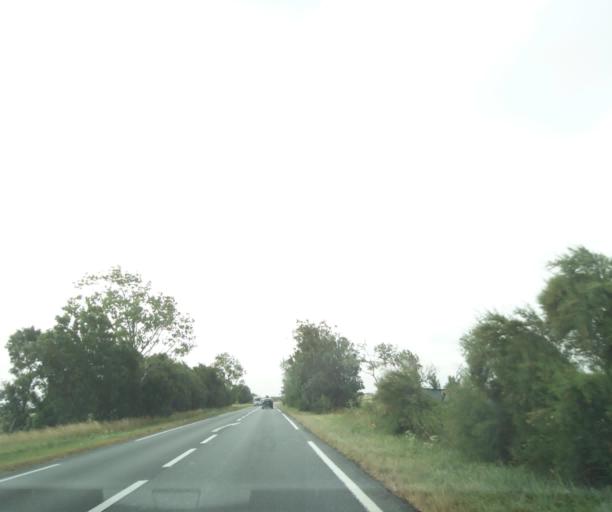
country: FR
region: Poitou-Charentes
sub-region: Departement de la Charente-Maritime
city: Andilly
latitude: 46.2566
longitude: -1.0665
